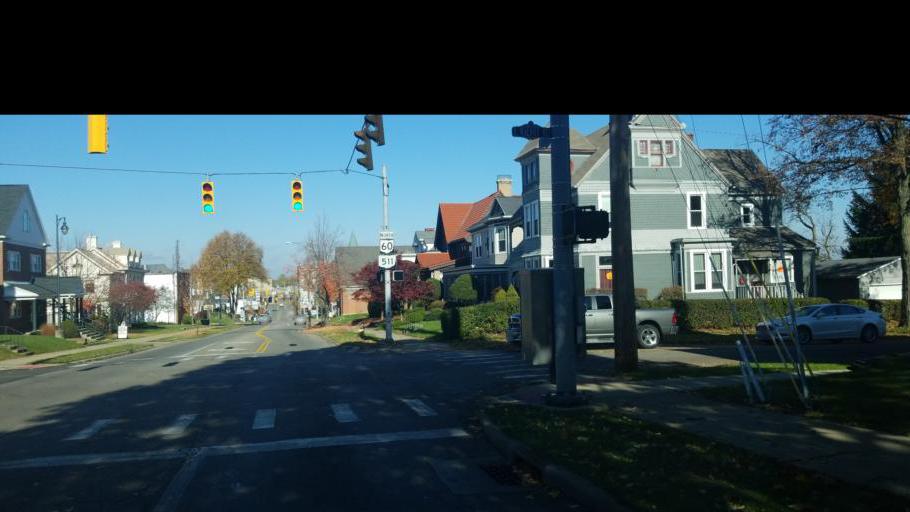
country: US
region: Ohio
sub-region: Ashland County
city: Ashland
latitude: 40.8653
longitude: -82.3135
